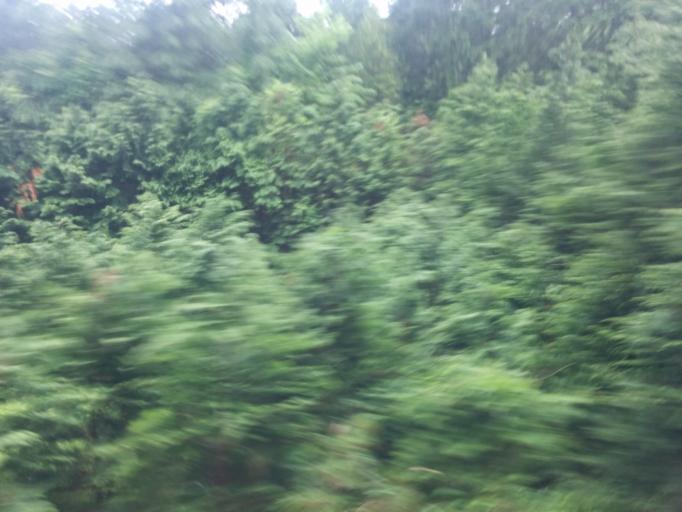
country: JP
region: Tochigi
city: Imaichi
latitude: 36.6662
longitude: 139.7223
